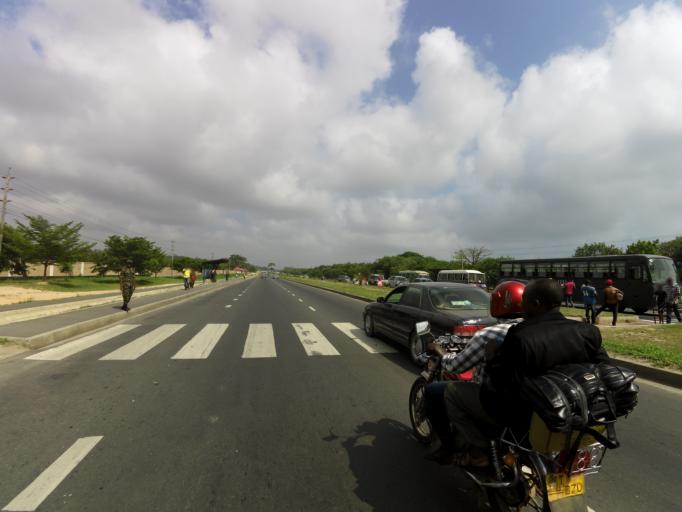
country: TZ
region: Dar es Salaam
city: Magomeni
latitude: -6.7574
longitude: 39.2246
